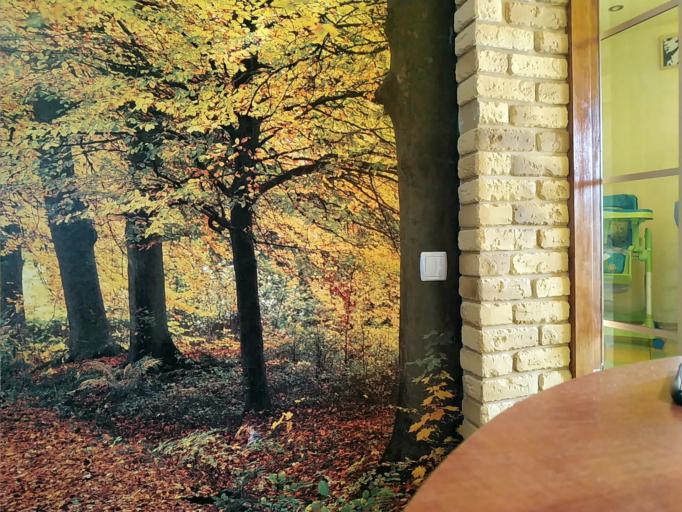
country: RU
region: Novgorod
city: Parfino
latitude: 57.7969
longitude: 31.6263
